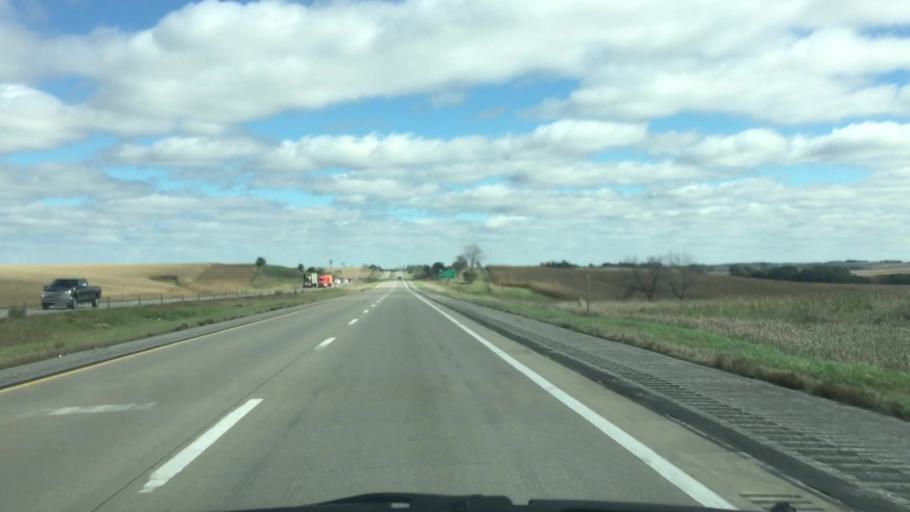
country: US
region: Iowa
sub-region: Iowa County
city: Williamsburg
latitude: 41.6914
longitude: -92.0971
